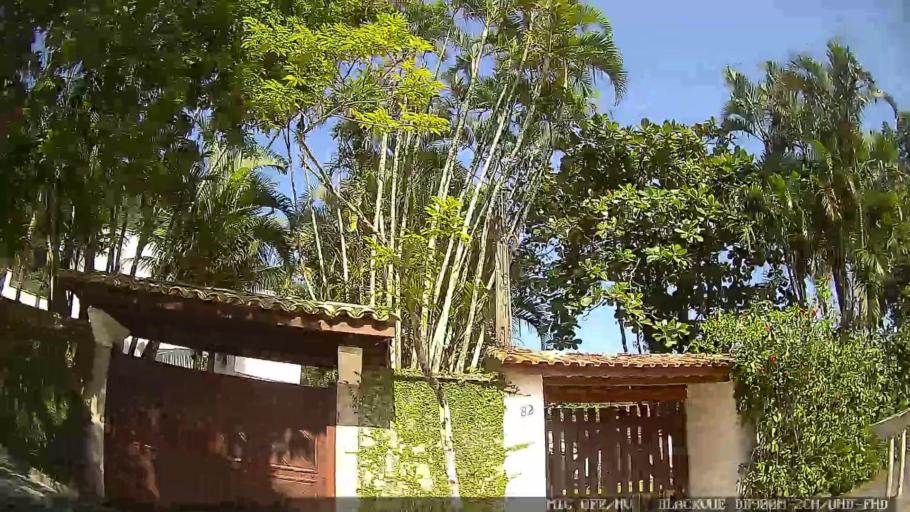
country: BR
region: Sao Paulo
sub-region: Guaruja
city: Guaruja
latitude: -24.0177
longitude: -46.2876
